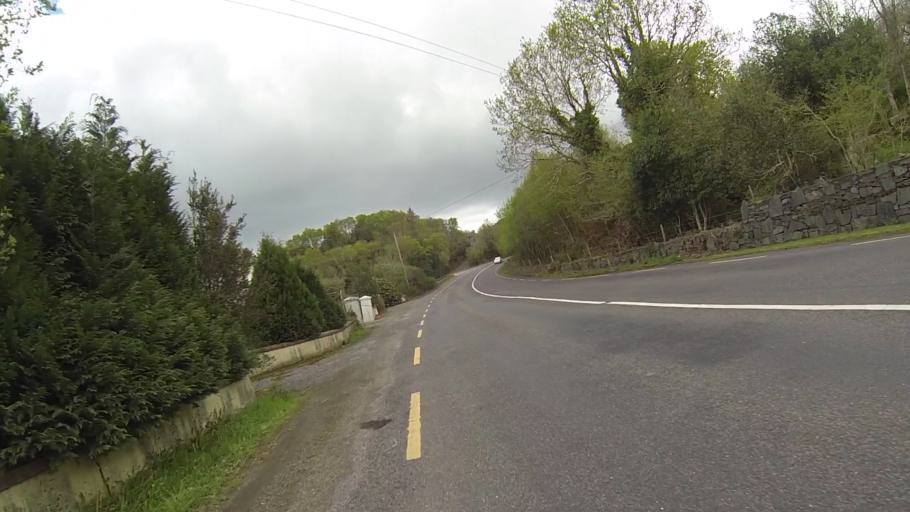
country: IE
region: Munster
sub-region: County Cork
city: Bantry
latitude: 51.7340
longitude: -9.5591
